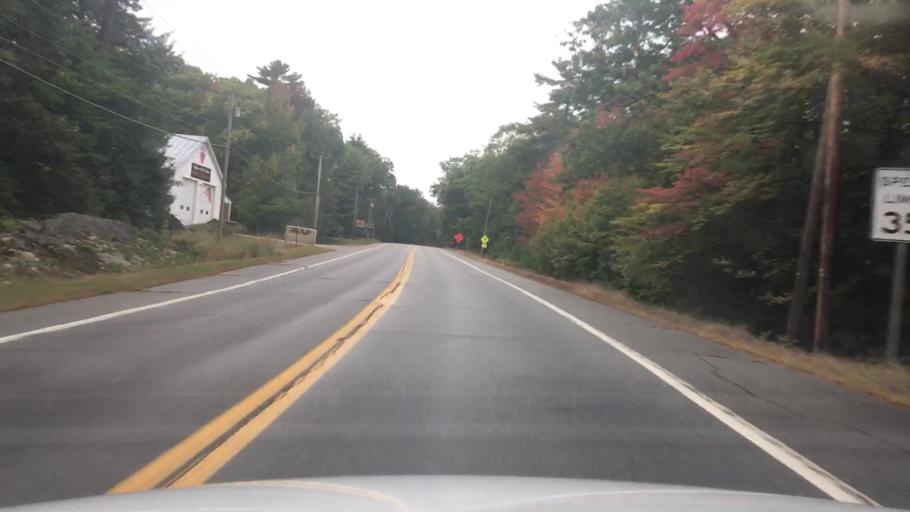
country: US
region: Maine
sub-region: Kennebec County
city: Rome
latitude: 44.5224
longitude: -69.8811
